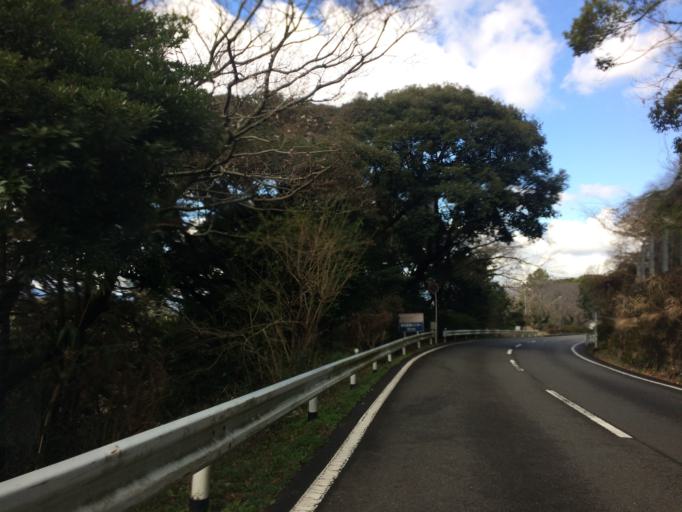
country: JP
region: Shizuoka
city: Shizuoka-shi
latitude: 34.9812
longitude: 138.4389
